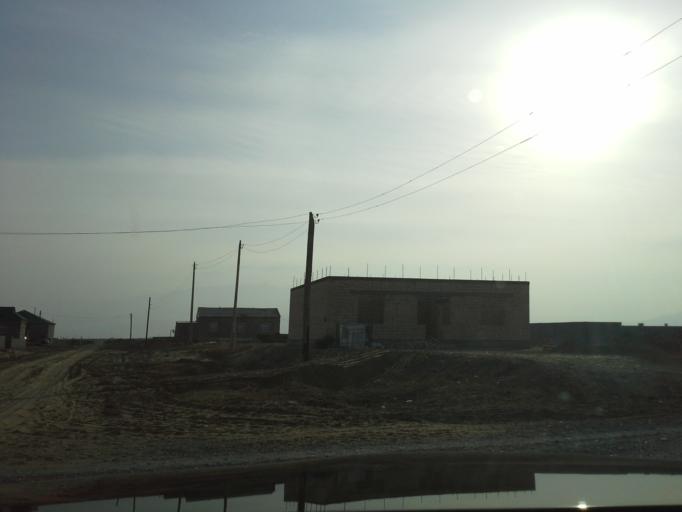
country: TM
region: Ahal
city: Abadan
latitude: 38.1722
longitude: 58.0388
